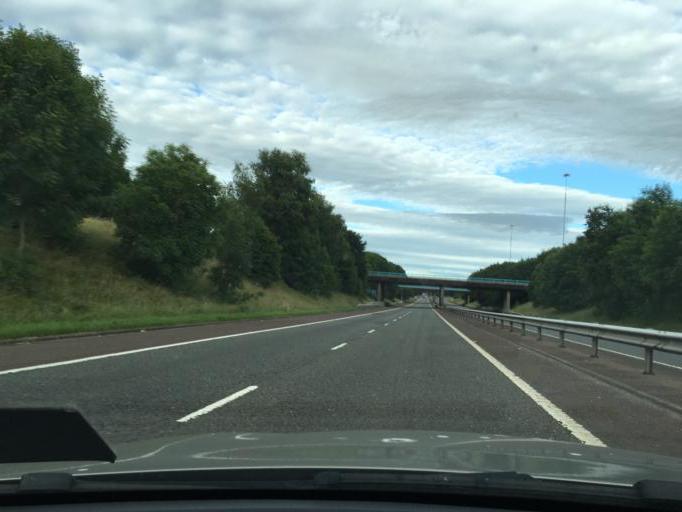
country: GB
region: Northern Ireland
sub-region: Antrim Borough
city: Antrim
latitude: 54.7448
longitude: -6.2394
